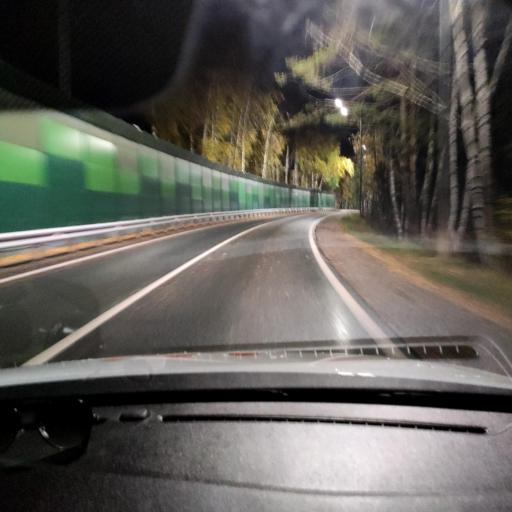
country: RU
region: Tatarstan
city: Verkhniy Uslon
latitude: 55.6285
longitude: 49.0142
